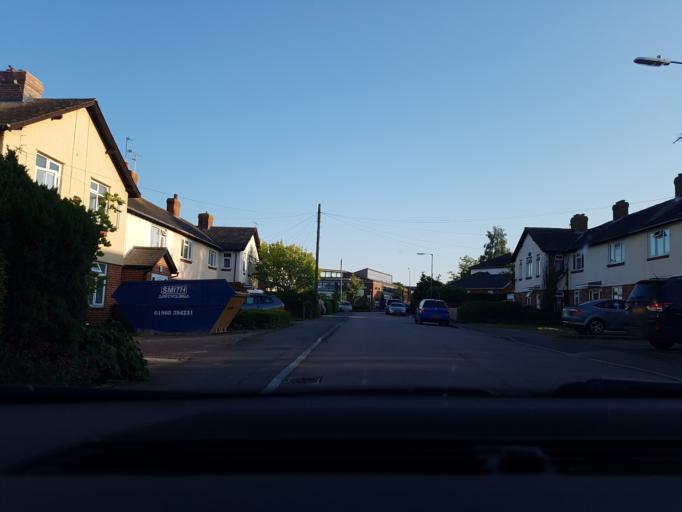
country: GB
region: England
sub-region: Buckinghamshire
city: Buckingham
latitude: 51.9958
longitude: -0.9828
